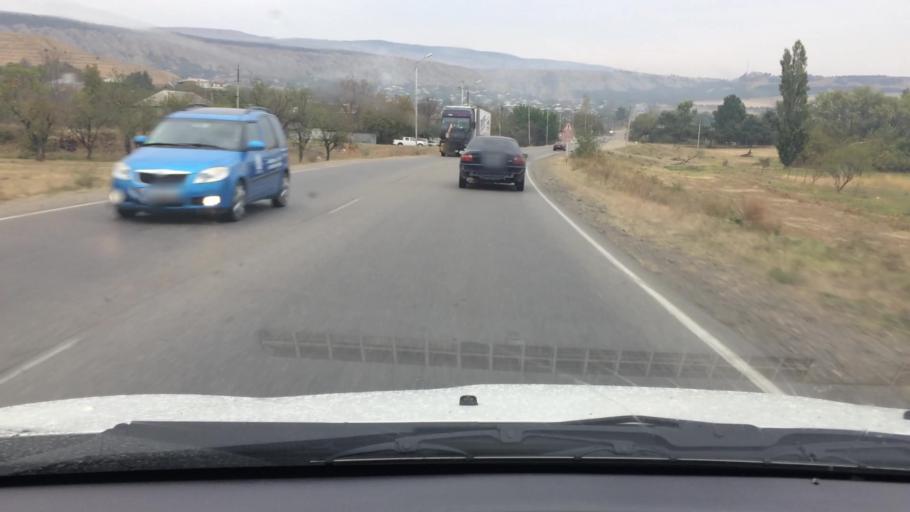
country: GE
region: T'bilisi
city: Tbilisi
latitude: 41.6023
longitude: 44.7791
